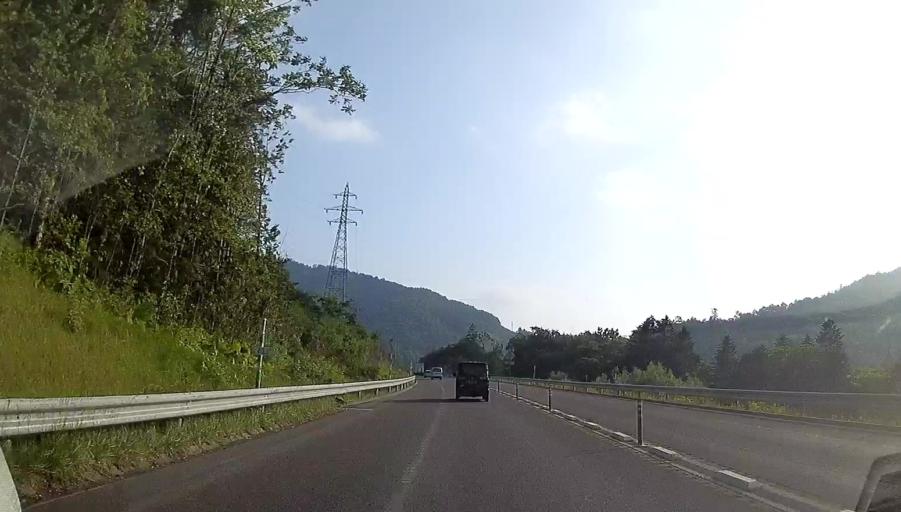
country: JP
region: Hokkaido
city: Shimo-furano
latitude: 43.0288
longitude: 142.4546
